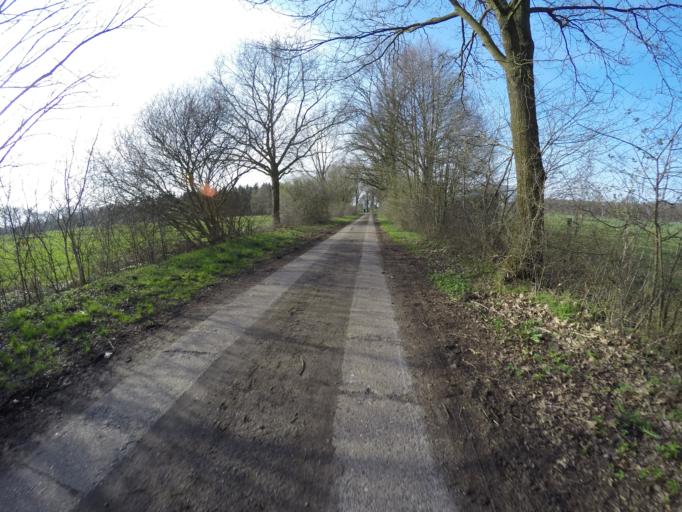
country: DE
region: Schleswig-Holstein
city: Bilsen
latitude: 53.7483
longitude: 9.8726
